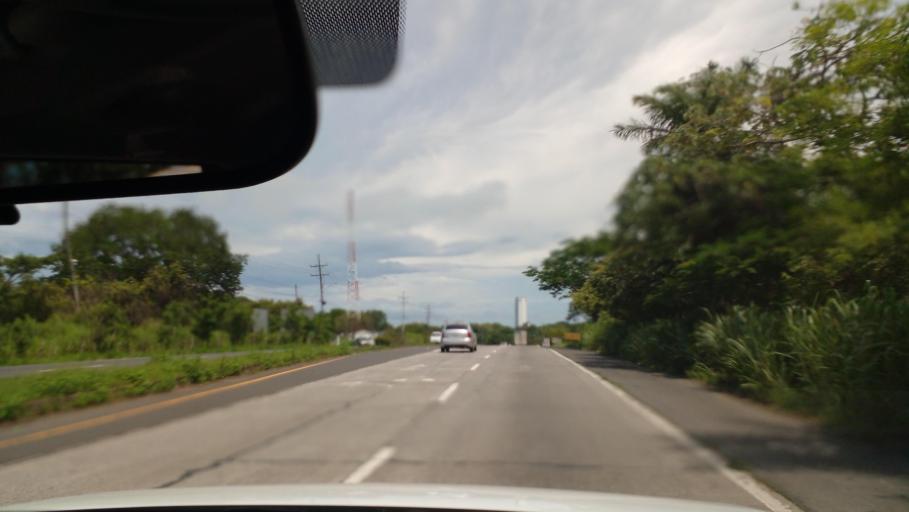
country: PA
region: Panama
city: Nueva Gorgona
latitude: 8.4822
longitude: -79.9583
